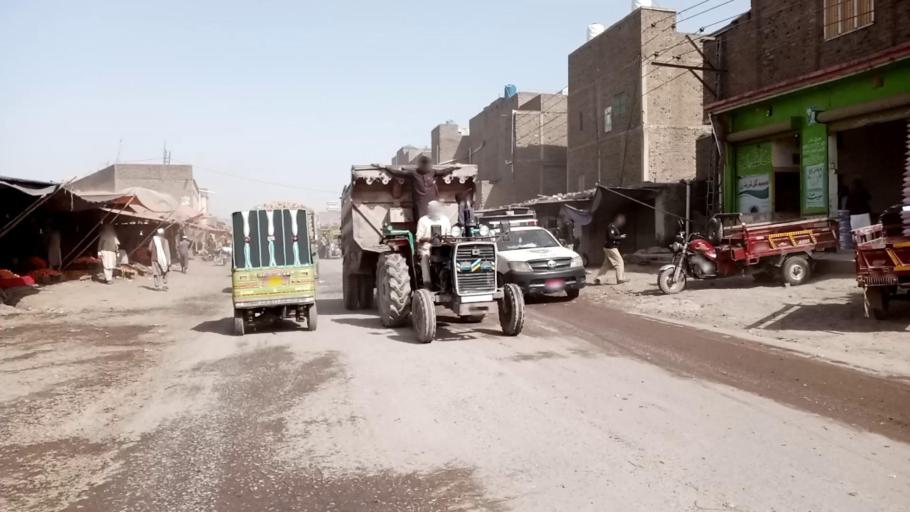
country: PK
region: Khyber Pakhtunkhwa
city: Peshawar
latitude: 33.9917
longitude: 71.6335
